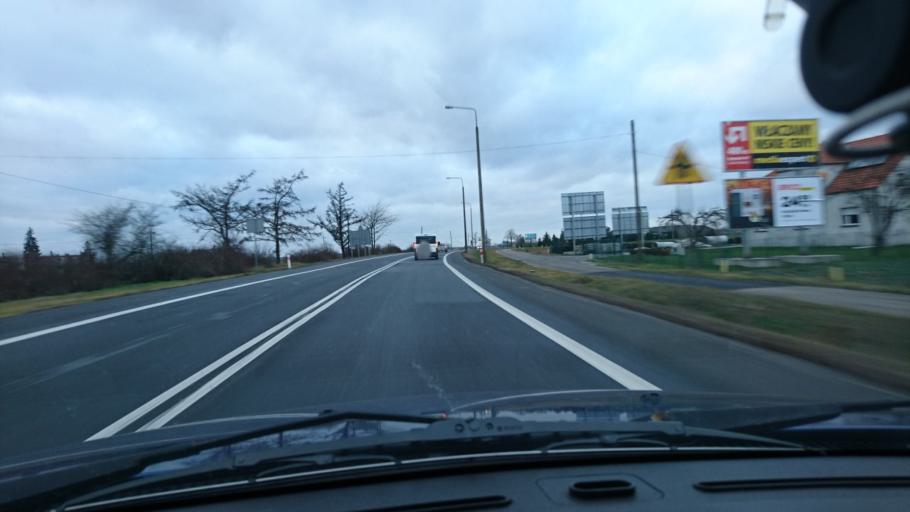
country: PL
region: Opole Voivodeship
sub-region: Powiat kluczborski
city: Kluczbork
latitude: 50.9941
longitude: 18.2097
